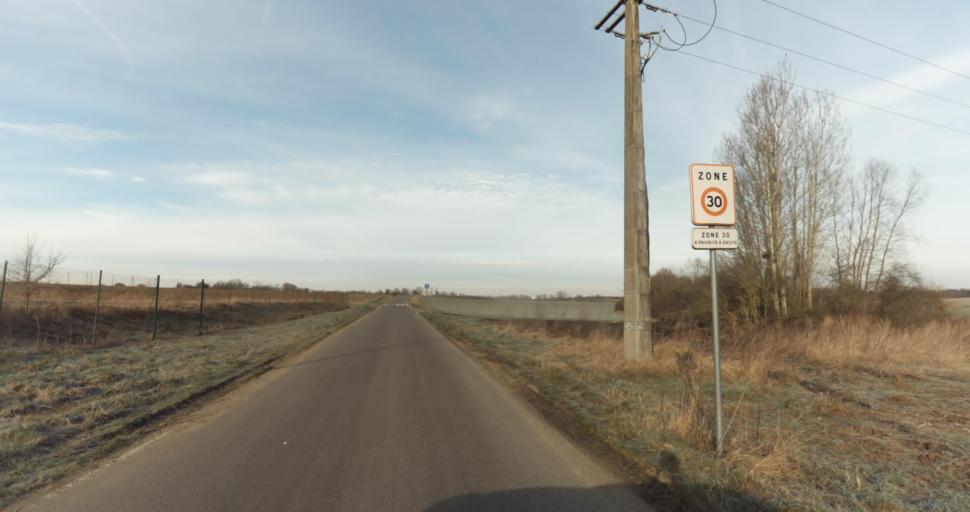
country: FR
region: Lorraine
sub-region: Departement de Meurthe-et-Moselle
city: Giraumont
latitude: 49.1595
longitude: 5.9027
